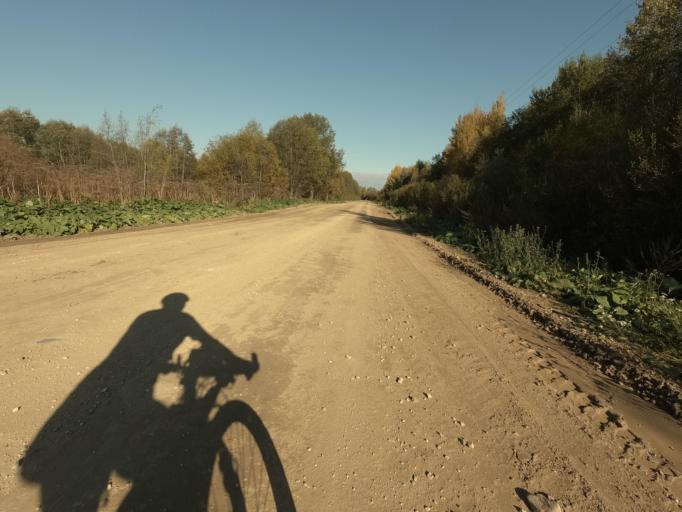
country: RU
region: Novgorod
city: Batetskiy
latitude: 58.8767
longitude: 30.7260
